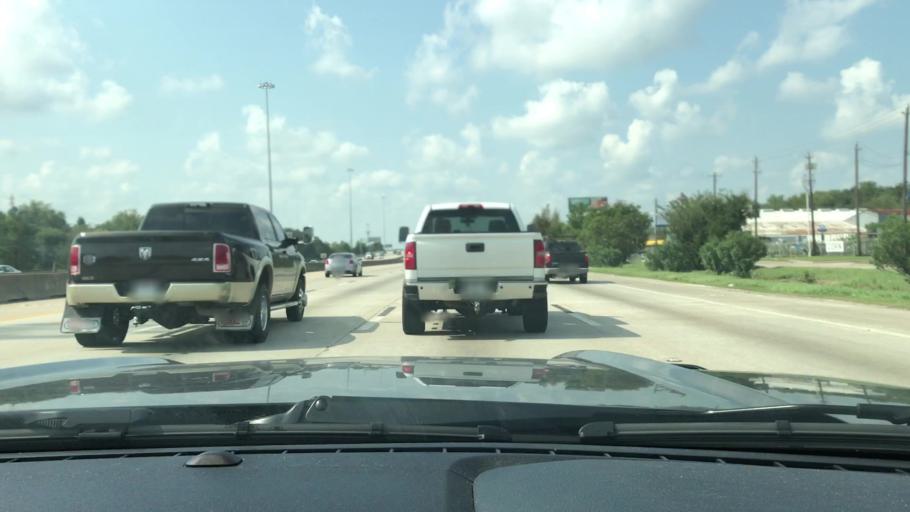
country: US
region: Texas
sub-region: Harris County
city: Aldine
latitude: 29.8855
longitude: -95.3214
